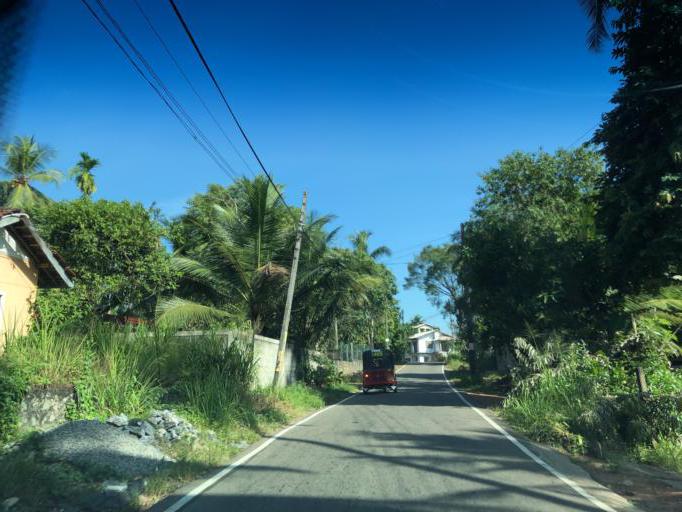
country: LK
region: Western
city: Homagama
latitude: 6.8013
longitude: 79.9804
